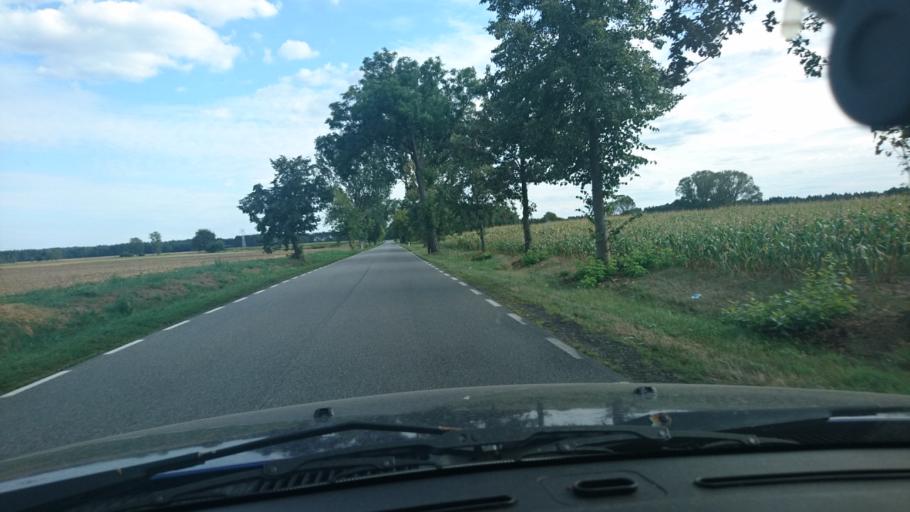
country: PL
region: Greater Poland Voivodeship
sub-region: Powiat ostrowski
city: Odolanow
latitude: 51.5610
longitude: 17.6970
